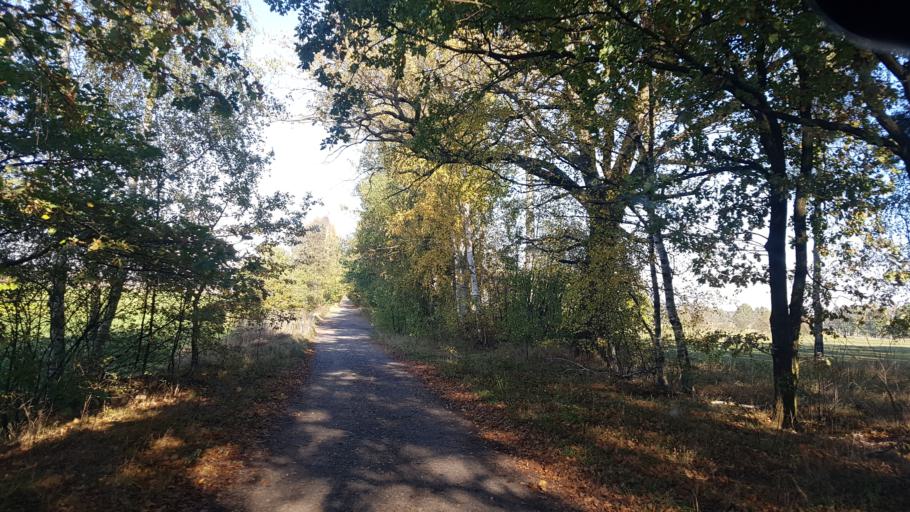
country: DE
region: Brandenburg
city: Ruckersdorf
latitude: 51.5546
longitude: 13.5397
